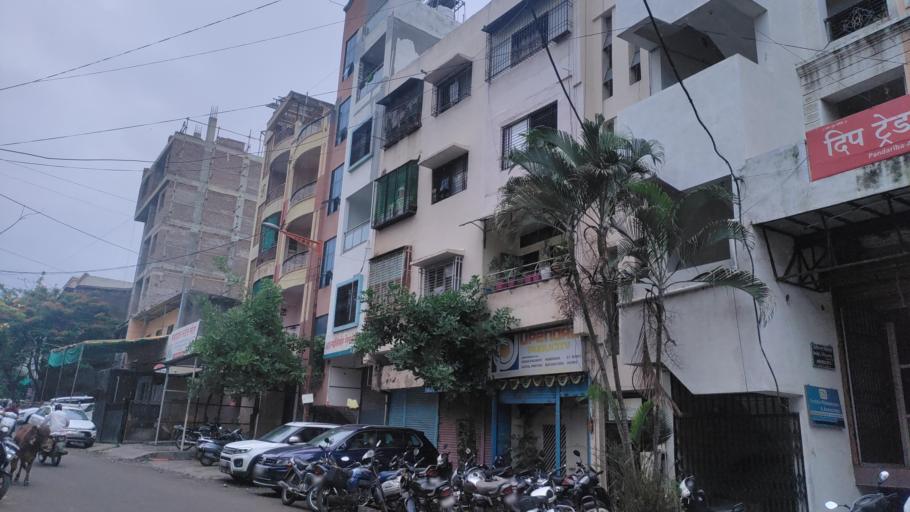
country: IN
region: Maharashtra
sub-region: Aurangabad Division
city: Aurangabad
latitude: 19.8858
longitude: 75.3325
